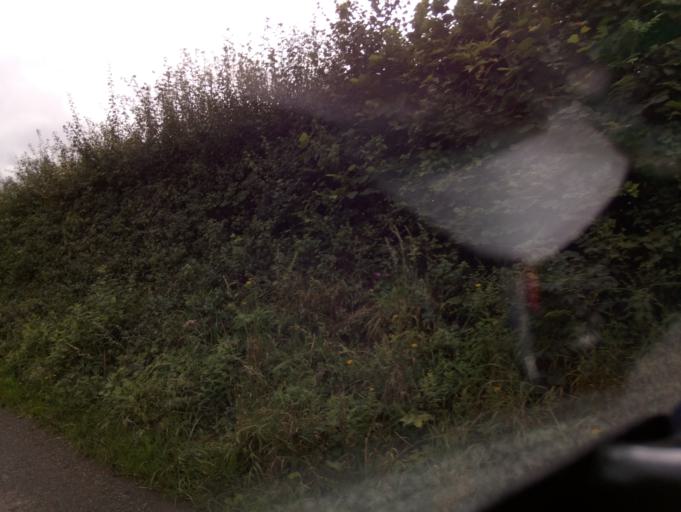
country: GB
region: England
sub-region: Devon
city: Kingsbridge
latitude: 50.2713
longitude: -3.7167
